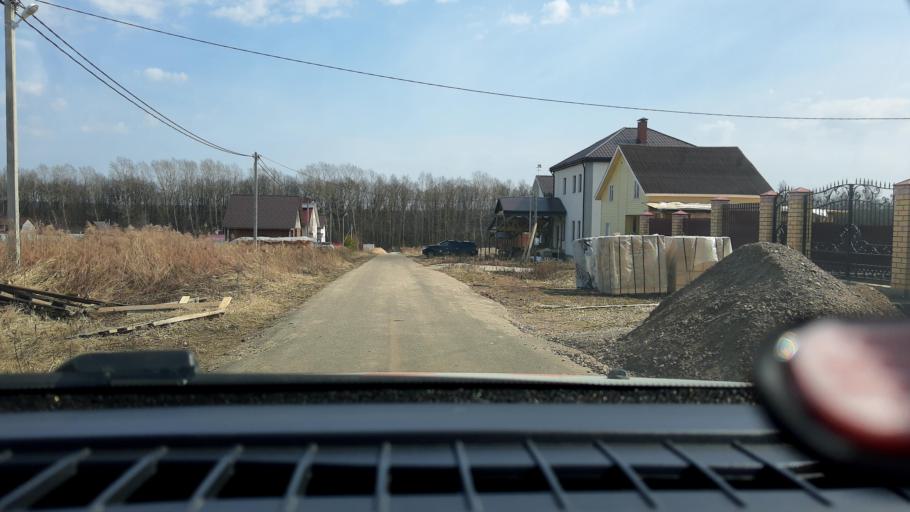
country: RU
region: Nizjnij Novgorod
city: Burevestnik
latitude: 56.0436
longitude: 43.8445
